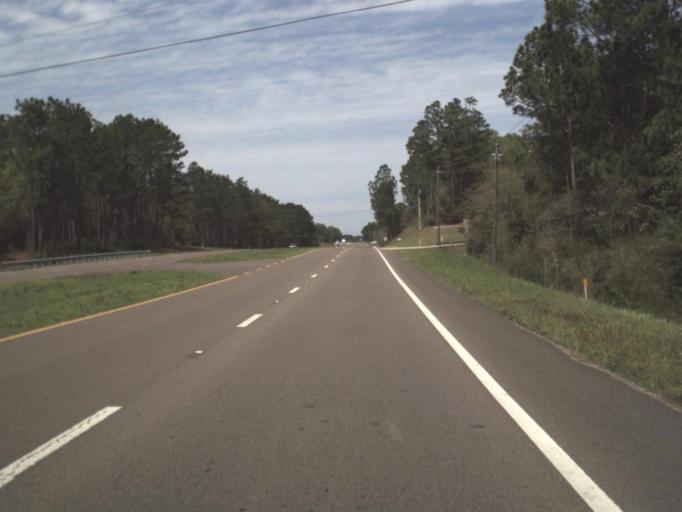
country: US
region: Florida
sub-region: Okaloosa County
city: Crestview
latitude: 30.7578
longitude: -86.5379
